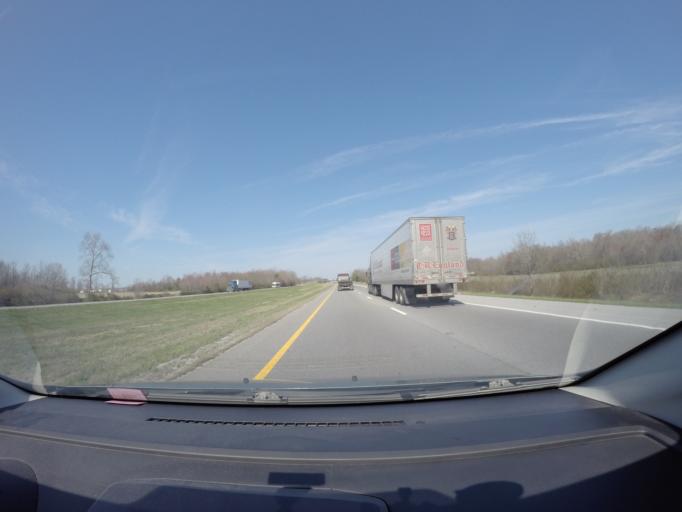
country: US
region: Tennessee
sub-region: Coffee County
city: New Union
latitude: 35.5323
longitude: -86.1552
